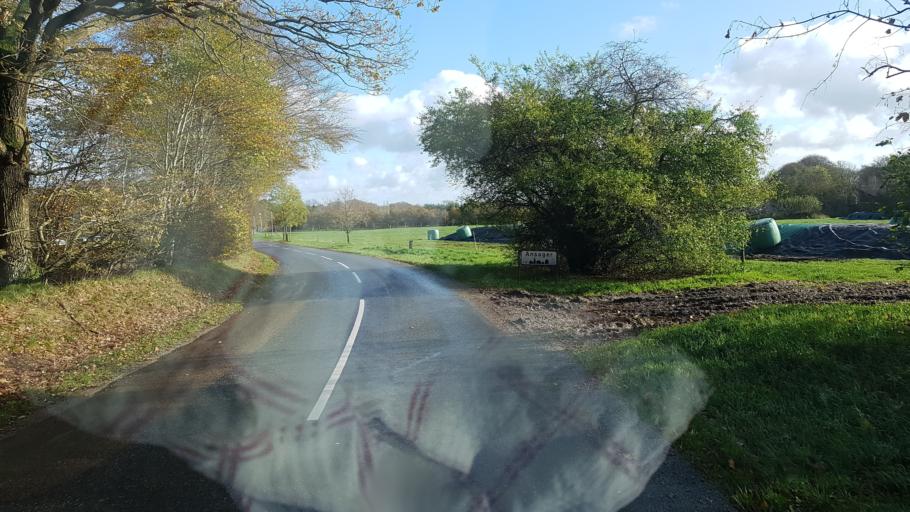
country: DK
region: South Denmark
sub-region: Varde Kommune
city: Olgod
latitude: 55.7005
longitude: 8.7433
